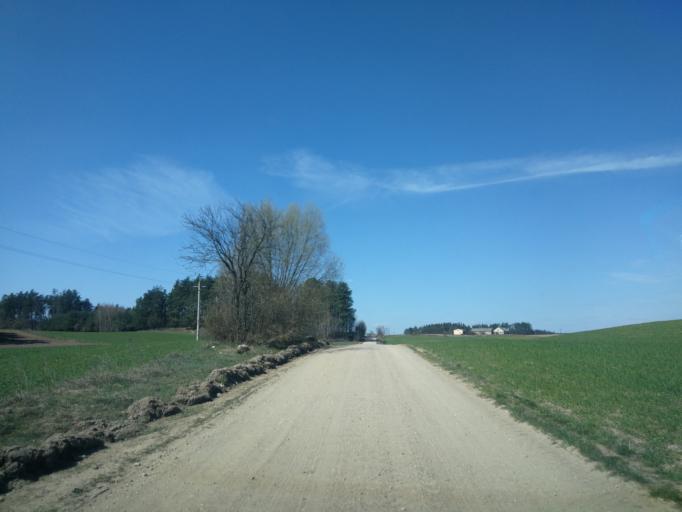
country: PL
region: Warmian-Masurian Voivodeship
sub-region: Powiat dzialdowski
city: Rybno
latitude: 53.4405
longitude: 19.9402
